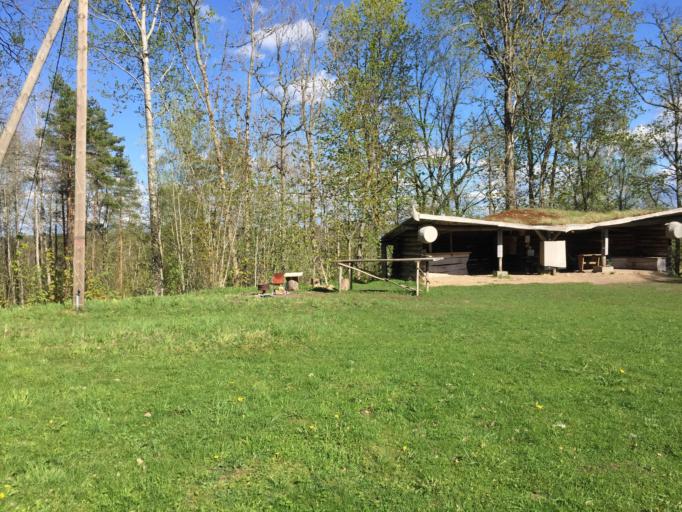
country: LV
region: Madonas Rajons
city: Madona
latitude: 56.8106
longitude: 26.0962
